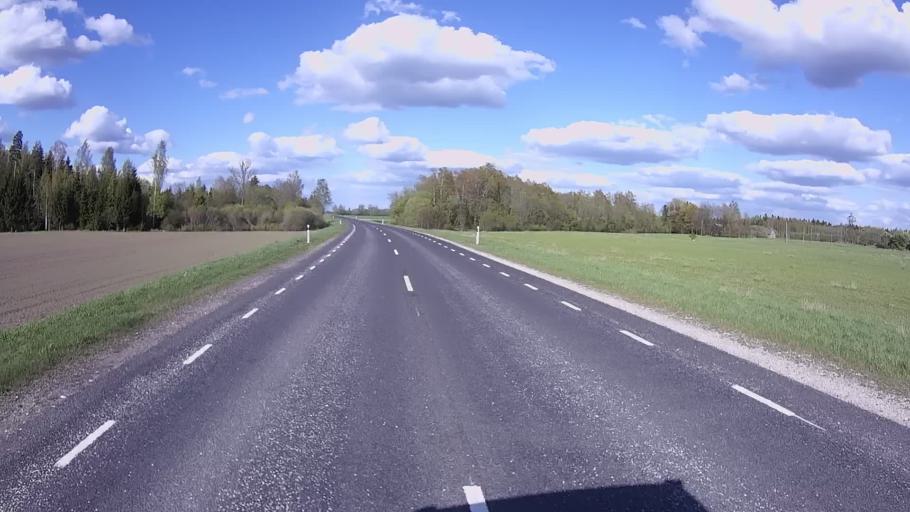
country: EE
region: Jogevamaa
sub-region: Poltsamaa linn
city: Poltsamaa
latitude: 58.7117
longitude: 26.1745
